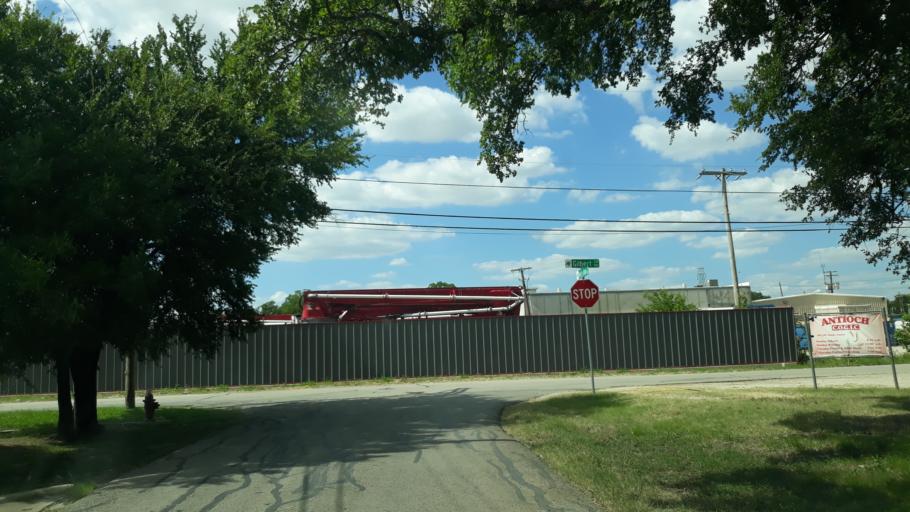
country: US
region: Texas
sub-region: Dallas County
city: Irving
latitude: 32.8142
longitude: -97.0041
